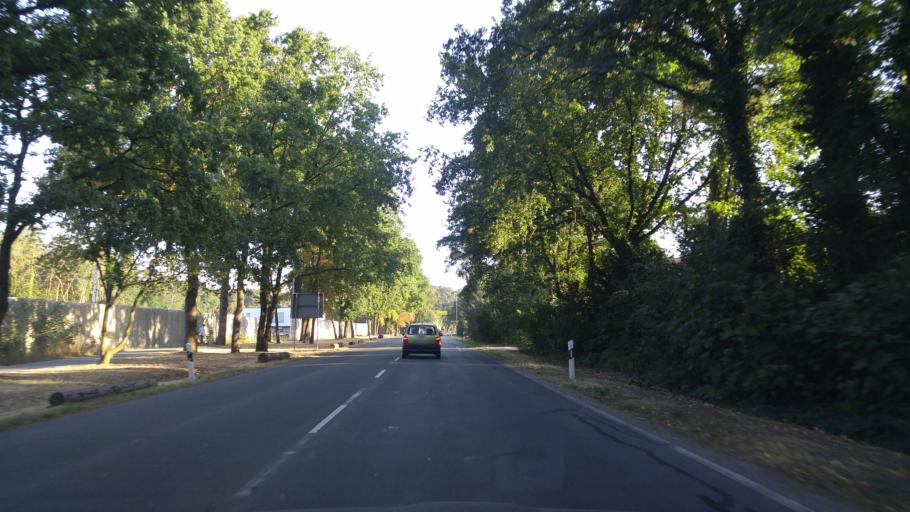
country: DE
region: Bavaria
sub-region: Regierungsbezirk Mittelfranken
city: Erlangen
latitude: 49.5455
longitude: 10.9854
